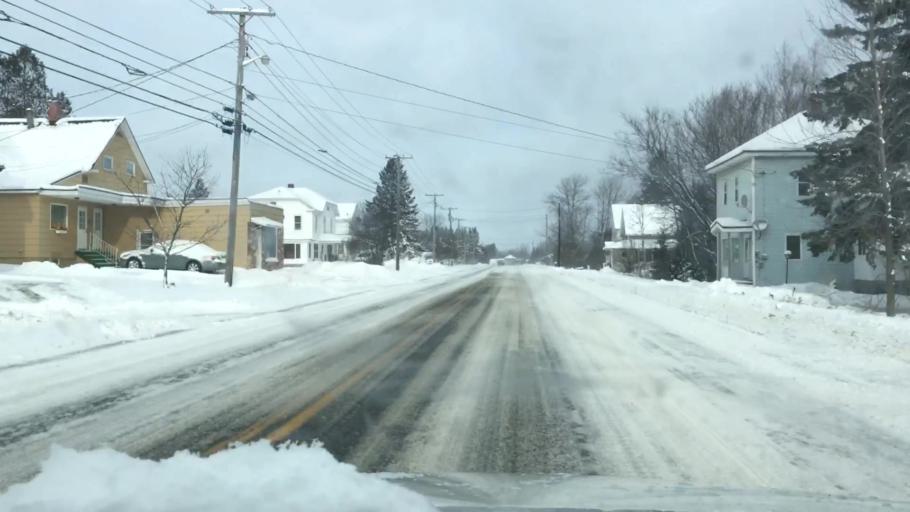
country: US
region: Maine
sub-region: Aroostook County
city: Van Buren
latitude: 47.1723
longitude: -67.9458
